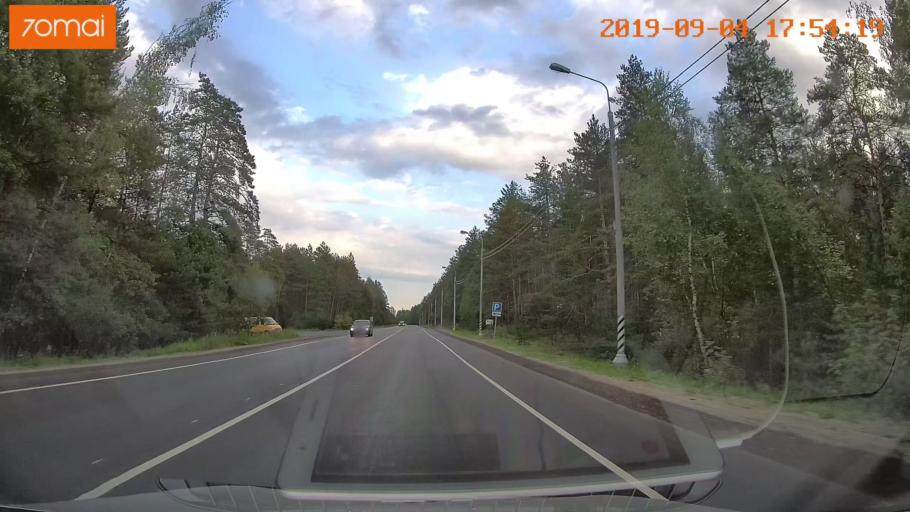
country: RU
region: Moskovskaya
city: Imeni Tsyurupy
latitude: 55.5112
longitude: 38.7417
